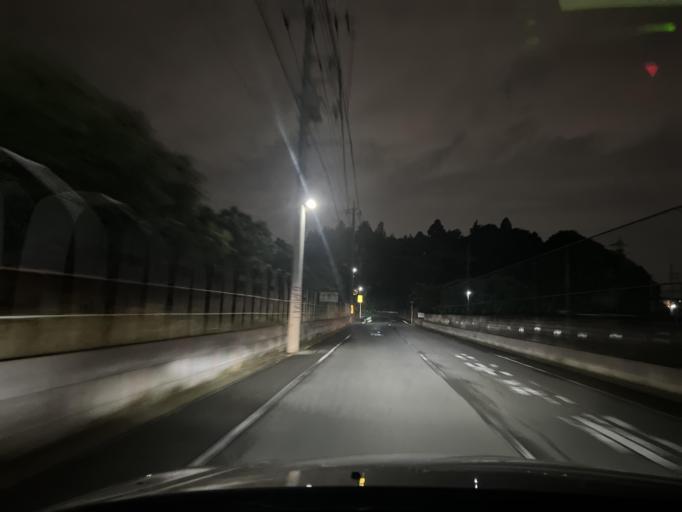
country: JP
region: Chiba
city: Kashiwa
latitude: 35.8384
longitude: 139.9377
